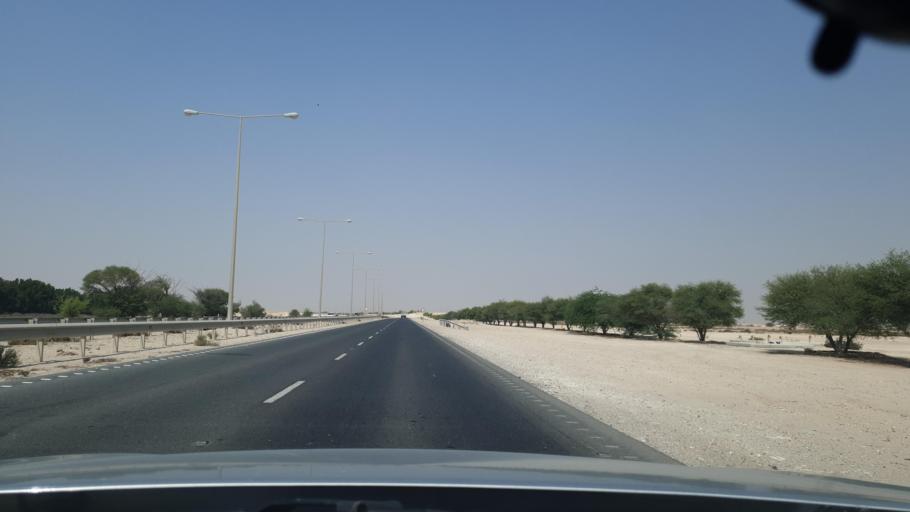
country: QA
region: Al Khawr
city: Al Khawr
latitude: 25.7302
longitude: 51.4949
